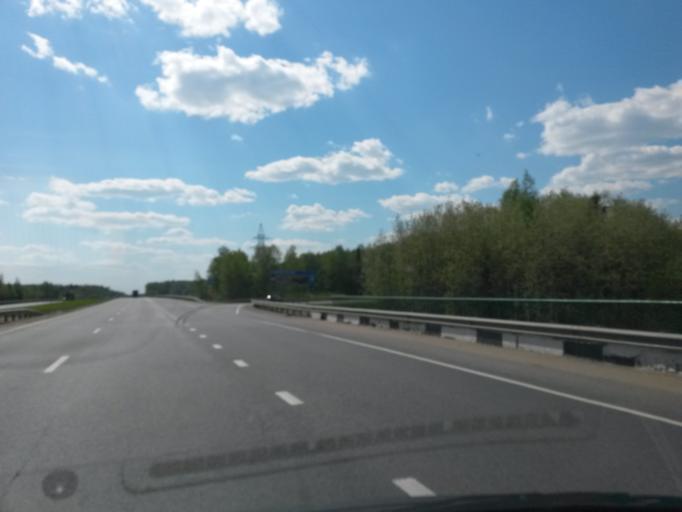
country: RU
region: Jaroslavl
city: Krasnyye Tkachi
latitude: 57.4056
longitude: 39.6560
